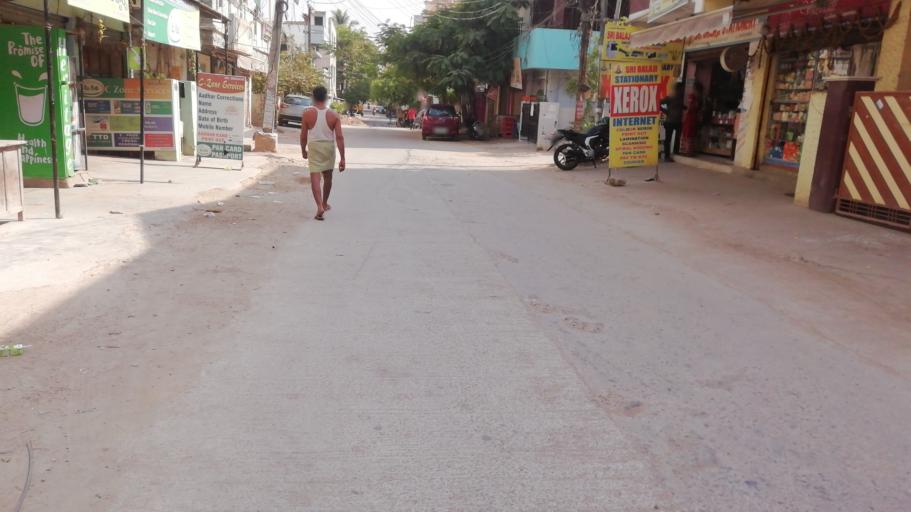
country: IN
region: Telangana
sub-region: Rangareddi
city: Gaddi Annaram
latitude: 17.3670
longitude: 78.5330
